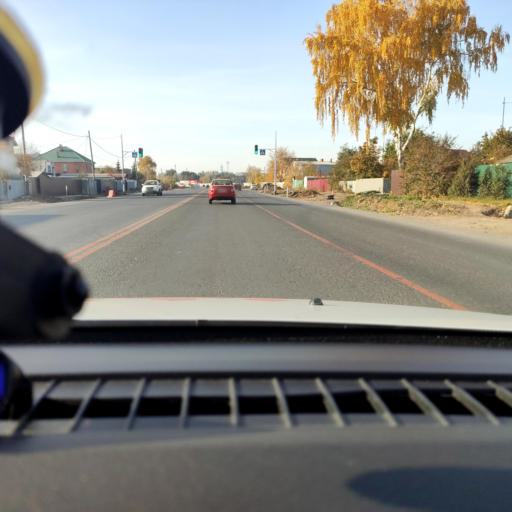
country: RU
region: Samara
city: Samara
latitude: 53.1306
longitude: 50.0941
